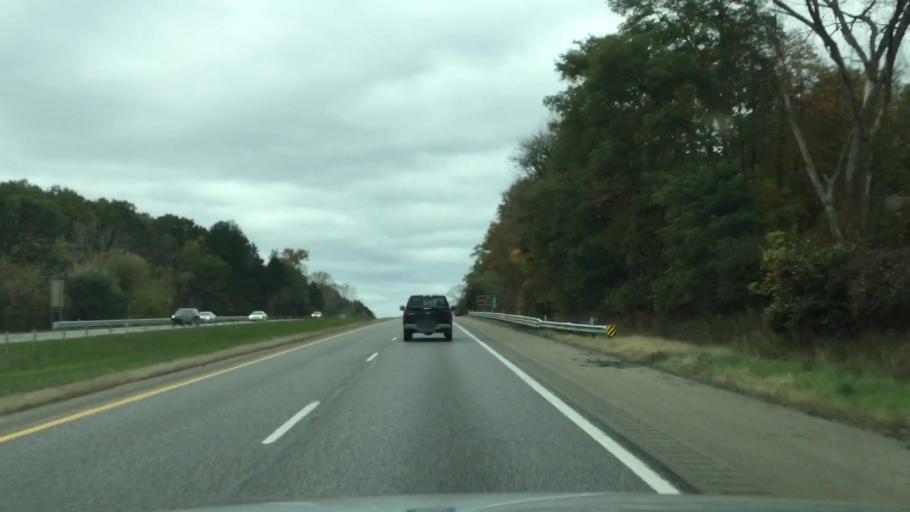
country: US
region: Michigan
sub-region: Washtenaw County
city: Chelsea
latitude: 42.2936
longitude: -84.0543
